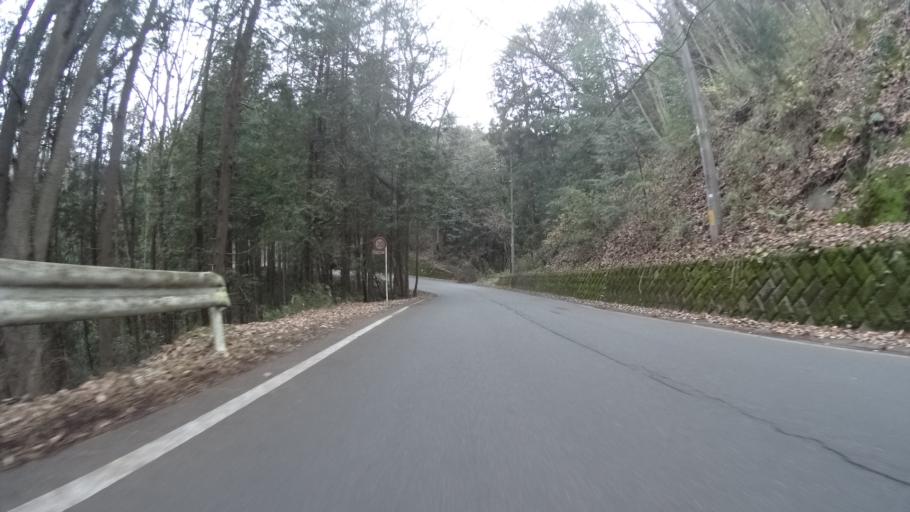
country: JP
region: Yamanashi
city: Uenohara
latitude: 35.6388
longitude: 139.1266
